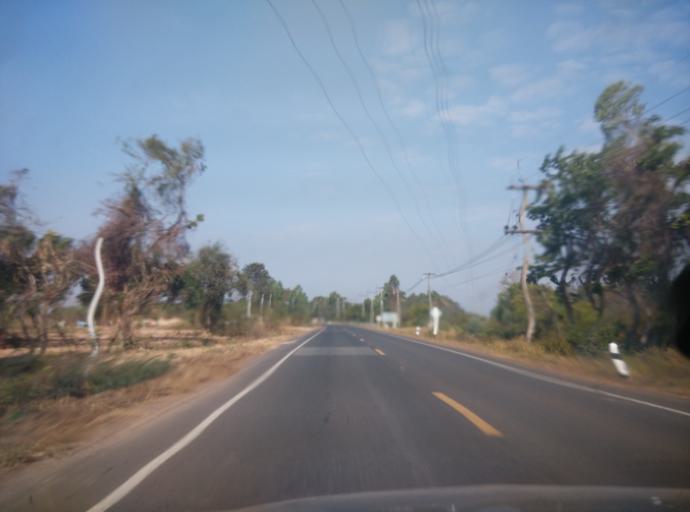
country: TH
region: Sisaket
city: Si Sa Ket
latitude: 15.1129
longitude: 104.2684
